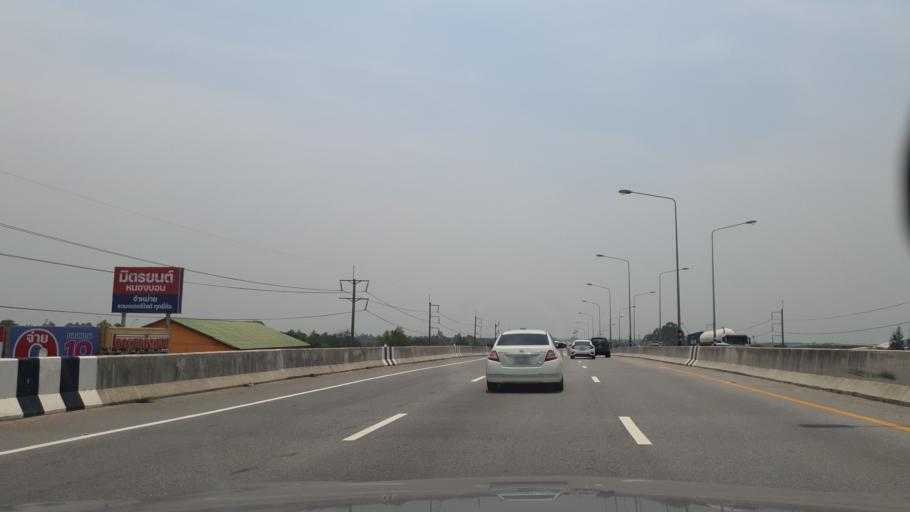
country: TH
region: Rayong
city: Nikhom Phattana
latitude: 12.8113
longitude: 101.1411
